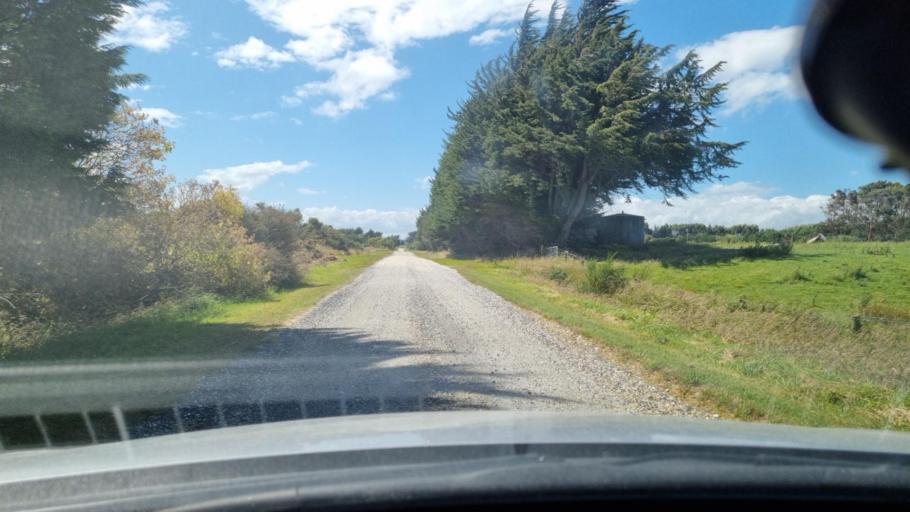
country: NZ
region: Southland
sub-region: Invercargill City
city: Invercargill
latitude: -46.4378
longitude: 168.3896
